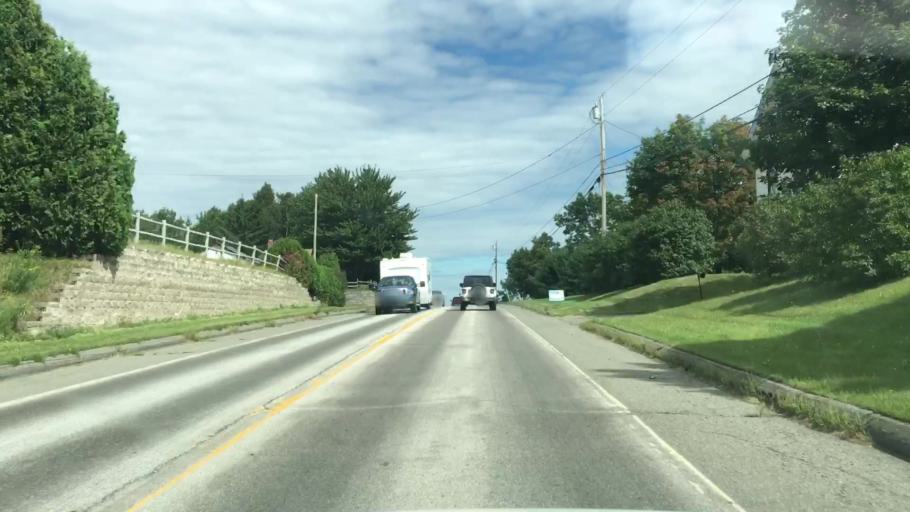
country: US
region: Maine
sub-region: Piscataquis County
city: Dover-Foxcroft
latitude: 45.1630
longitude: -69.2312
